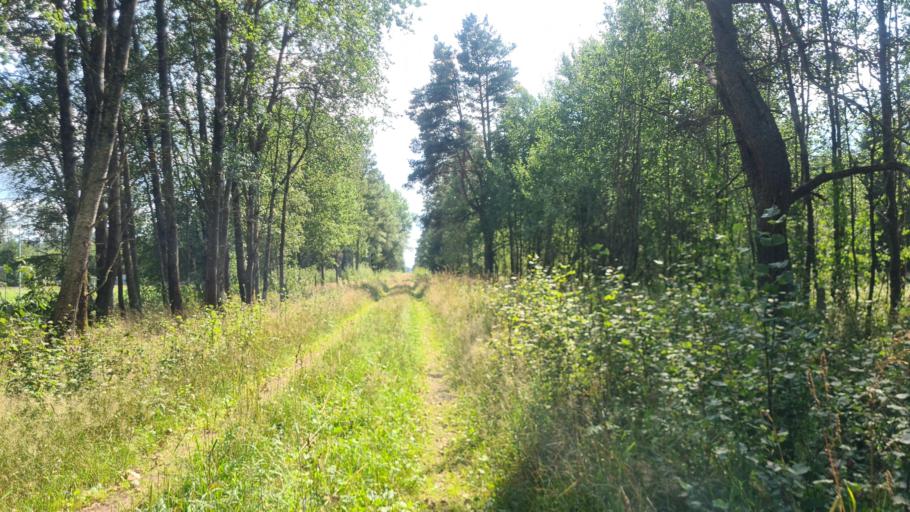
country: SE
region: Kronoberg
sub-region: Ljungby Kommun
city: Ljungby
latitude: 56.7636
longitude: 13.8922
